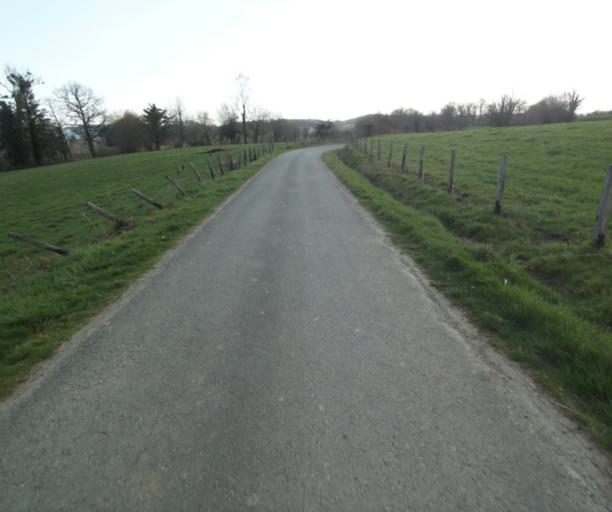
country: FR
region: Limousin
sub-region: Departement de la Correze
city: Saint-Mexant
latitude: 45.3402
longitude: 1.5997
